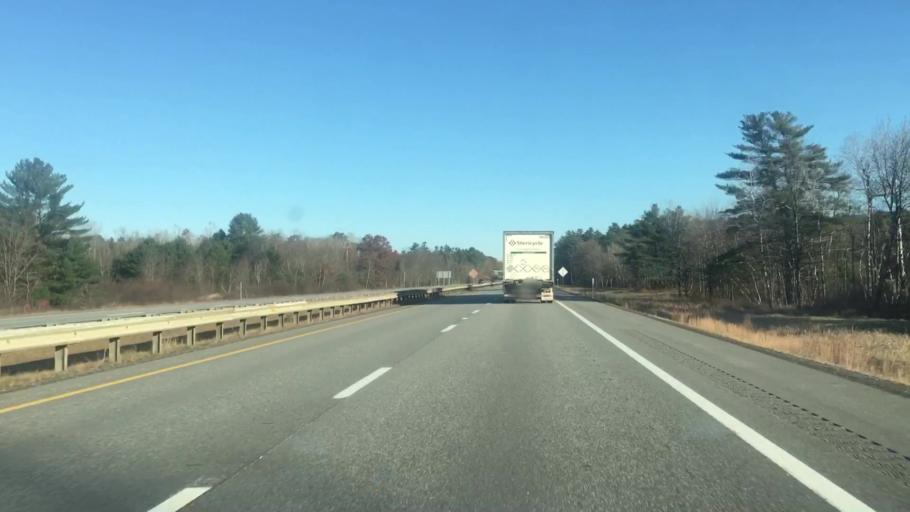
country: US
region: Maine
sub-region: Cumberland County
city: New Gloucester
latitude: 43.9129
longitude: -70.3390
